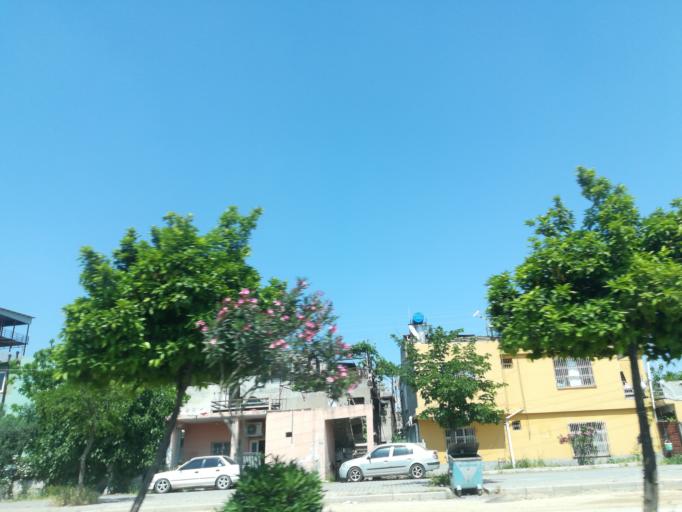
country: TR
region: Adana
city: Yuregir
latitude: 37.0143
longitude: 35.3862
